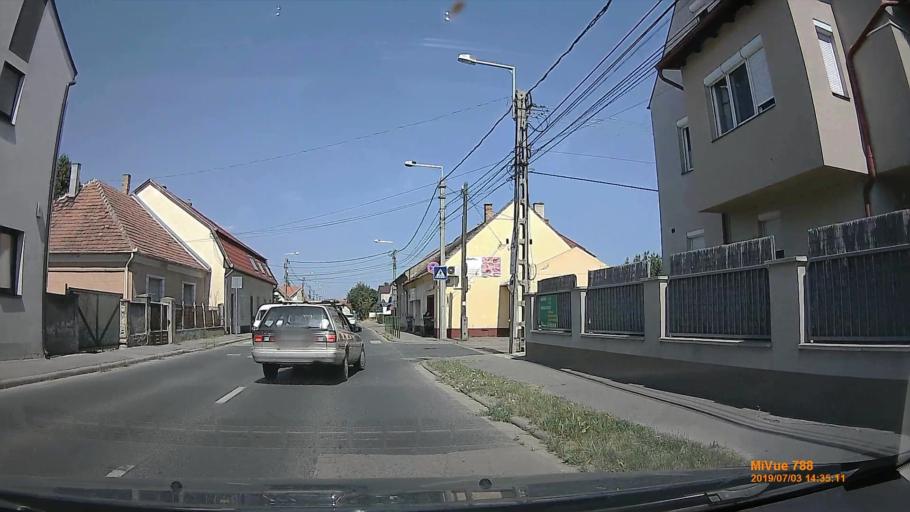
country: HU
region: Gyor-Moson-Sopron
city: Gyor
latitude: 47.6667
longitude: 17.6667
